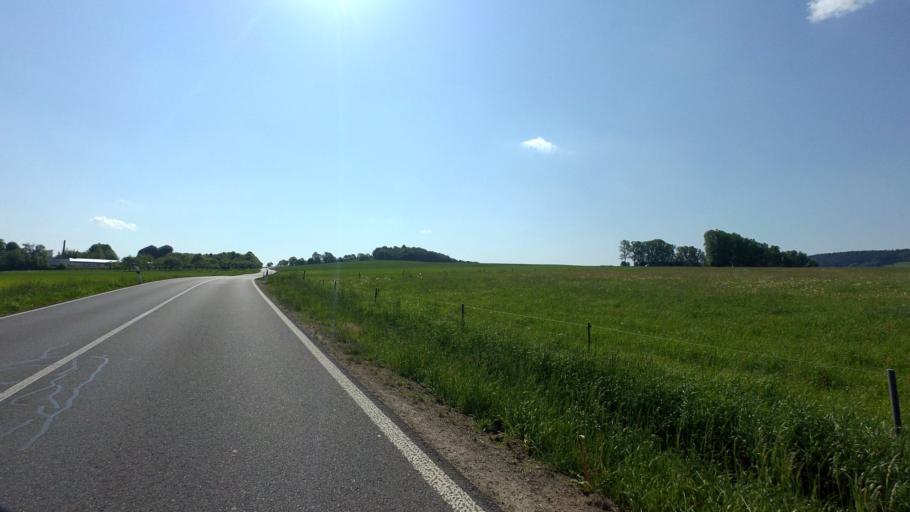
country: DE
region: Saxony
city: Neustadt in Sachsen
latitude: 51.0333
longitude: 14.1762
